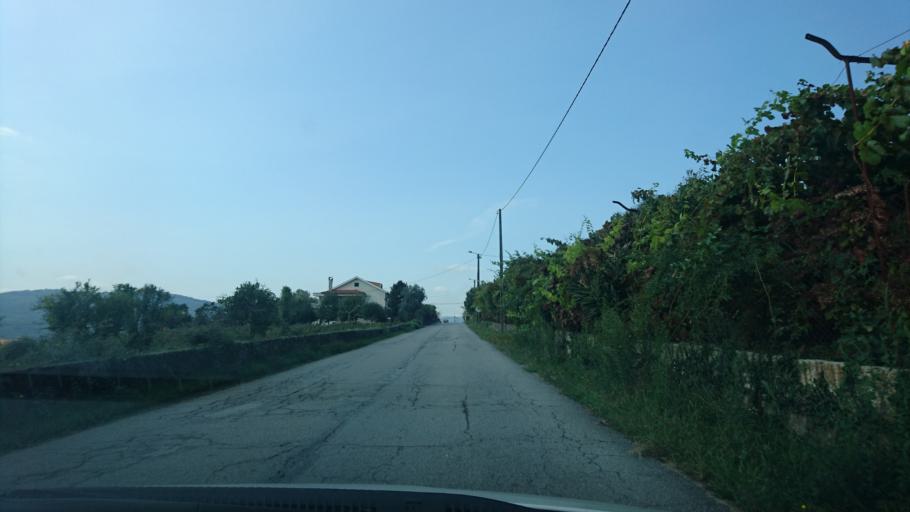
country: PT
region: Vila Real
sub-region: Mondim de Basto
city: Mondim de Basto
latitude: 41.4564
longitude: -7.9243
